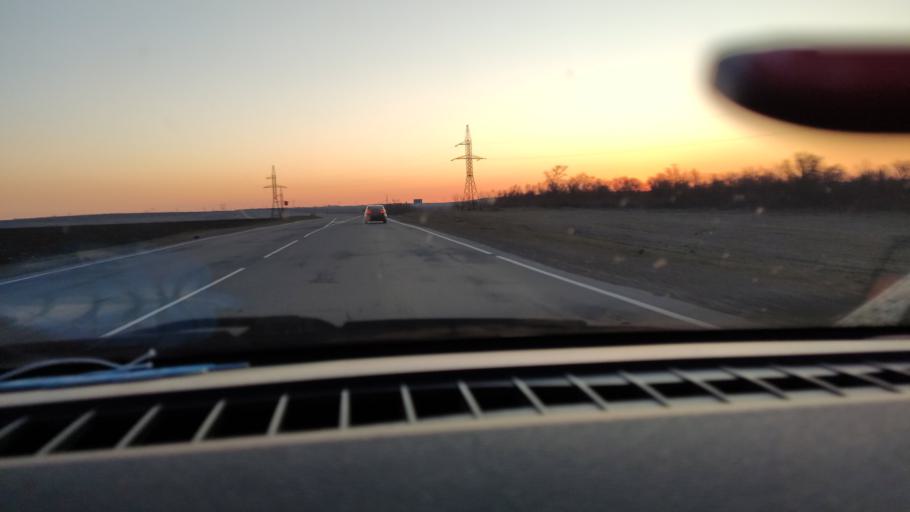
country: RU
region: Saratov
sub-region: Saratovskiy Rayon
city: Saratov
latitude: 51.7455
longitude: 46.0524
